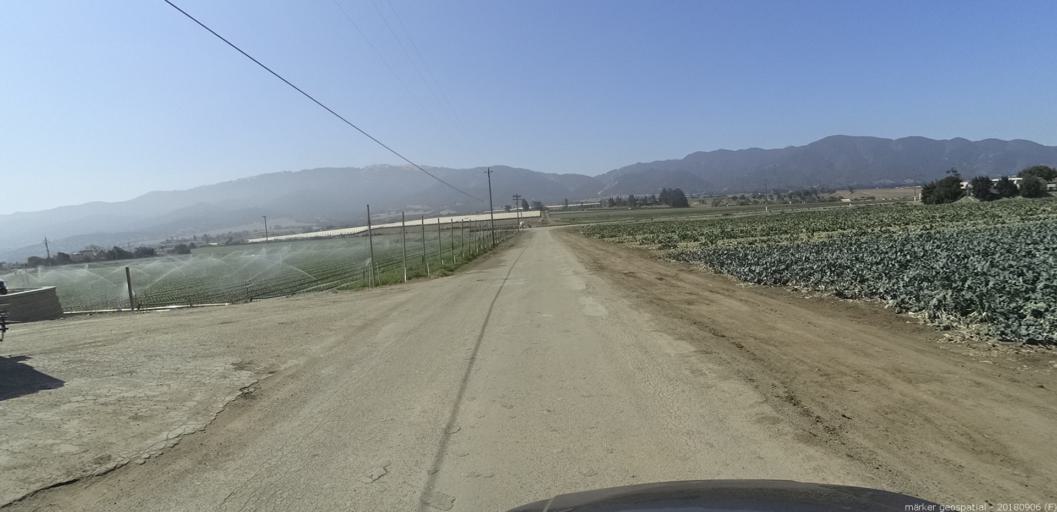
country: US
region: California
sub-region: Monterey County
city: Chualar
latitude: 36.5987
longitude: -121.6044
